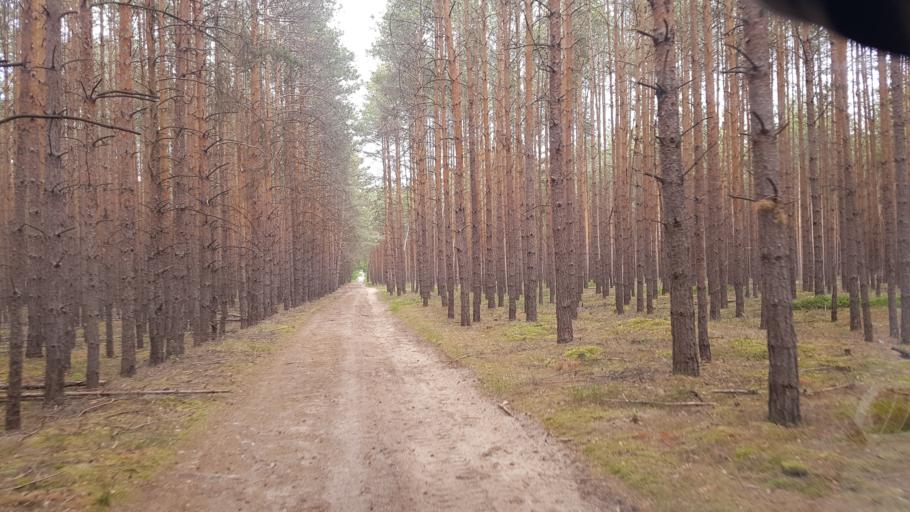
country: DE
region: Brandenburg
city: Finsterwalde
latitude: 51.6246
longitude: 13.6602
